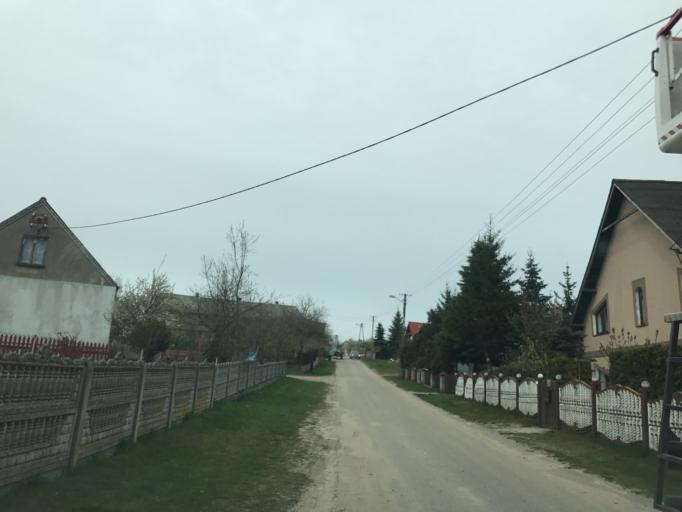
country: PL
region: Warmian-Masurian Voivodeship
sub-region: Powiat dzialdowski
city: Rybno
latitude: 53.3451
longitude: 19.8671
